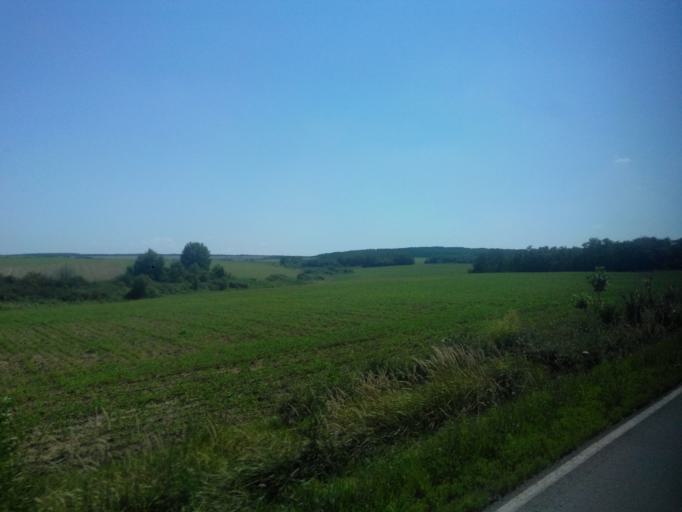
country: RO
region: Timis
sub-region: Comuna Barna
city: Barna
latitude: 45.7644
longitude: 22.0255
